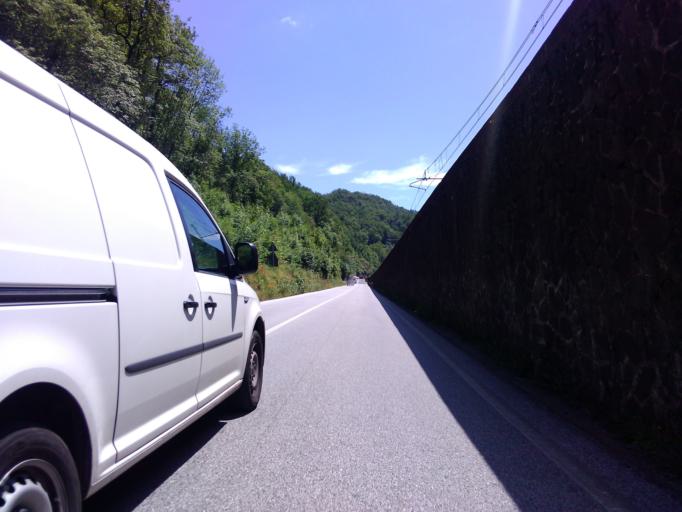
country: IT
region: Tuscany
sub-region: Provincia di Massa-Carrara
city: Villafranca in Lunigiana
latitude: 44.2781
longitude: 9.9525
